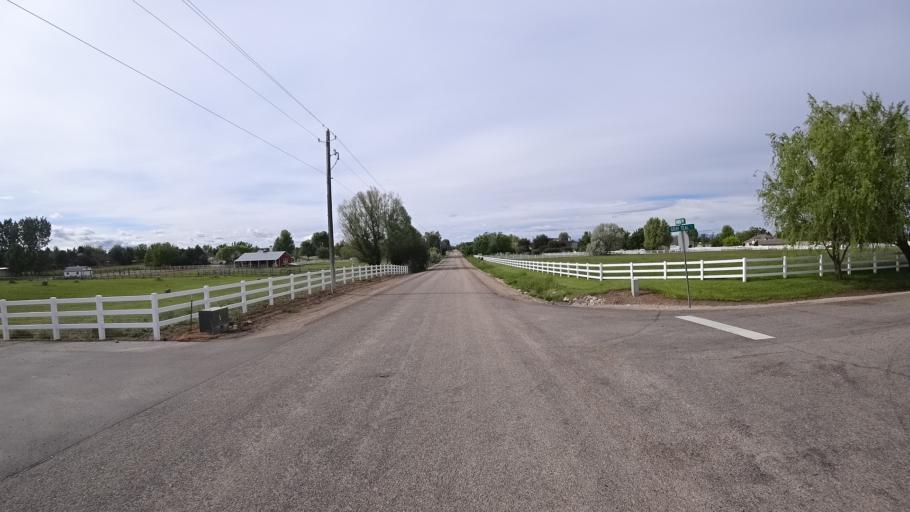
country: US
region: Idaho
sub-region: Ada County
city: Eagle
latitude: 43.7318
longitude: -116.4035
